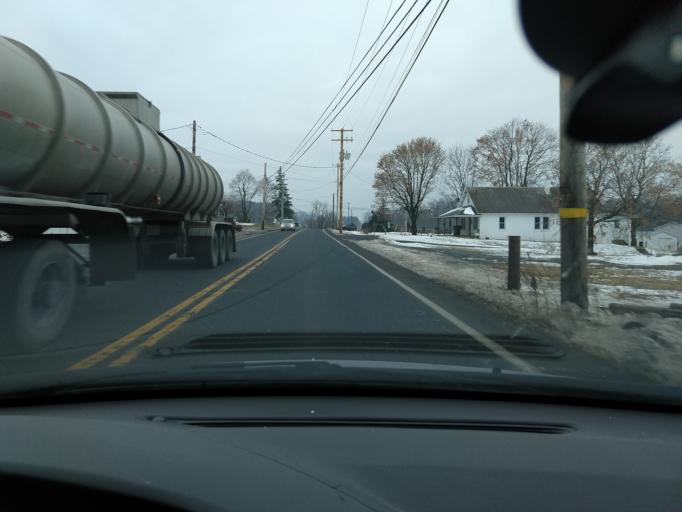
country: US
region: Pennsylvania
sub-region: Lehigh County
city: Macungie
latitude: 40.4790
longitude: -75.5282
